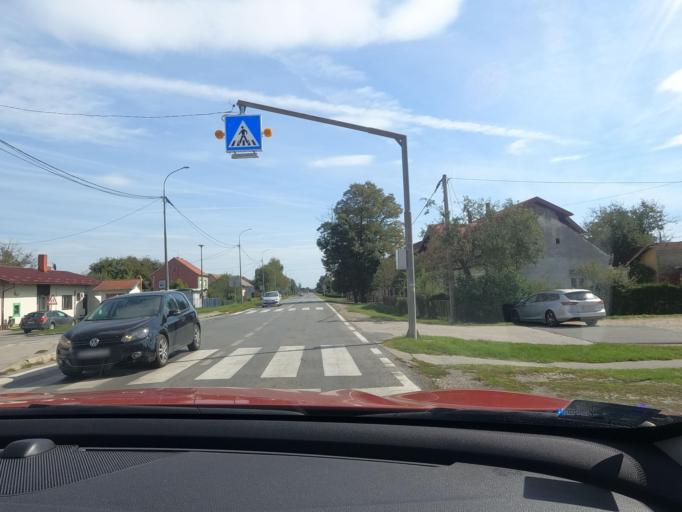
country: HR
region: Sisacko-Moslavacka
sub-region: Grad Sisak
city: Sisak
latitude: 45.4777
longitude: 16.4004
